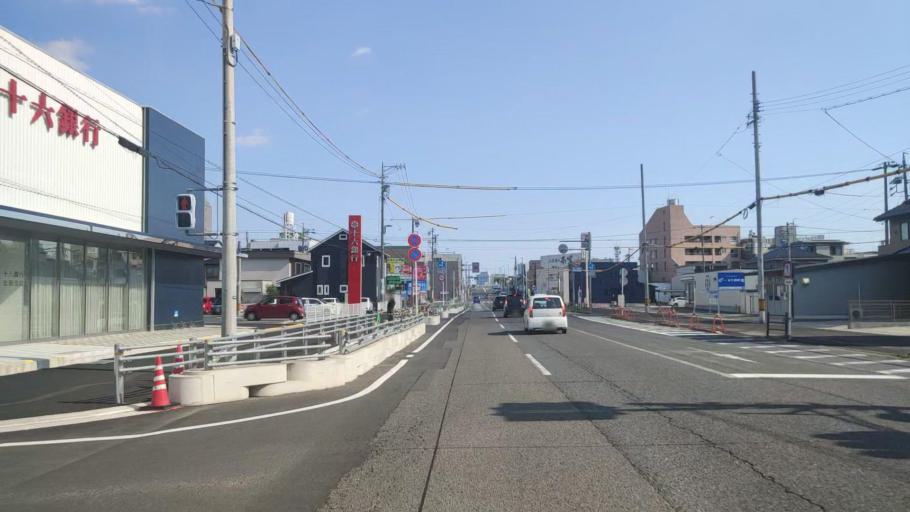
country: JP
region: Gifu
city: Gifu-shi
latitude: 35.4354
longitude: 136.7487
